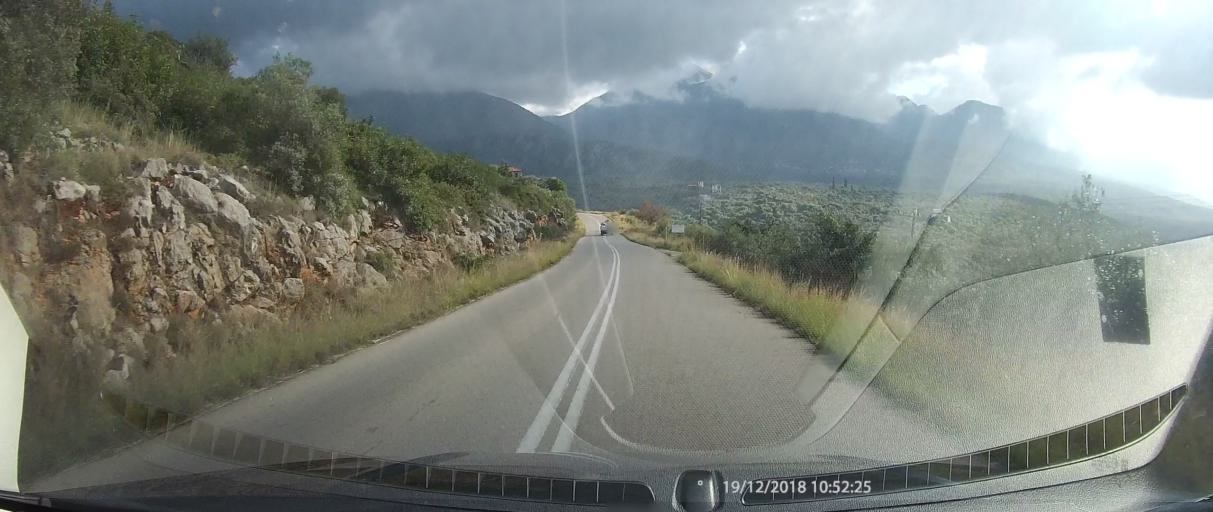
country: GR
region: Peloponnese
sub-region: Nomos Messinias
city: Kardamyli
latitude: 36.9133
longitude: 22.2267
